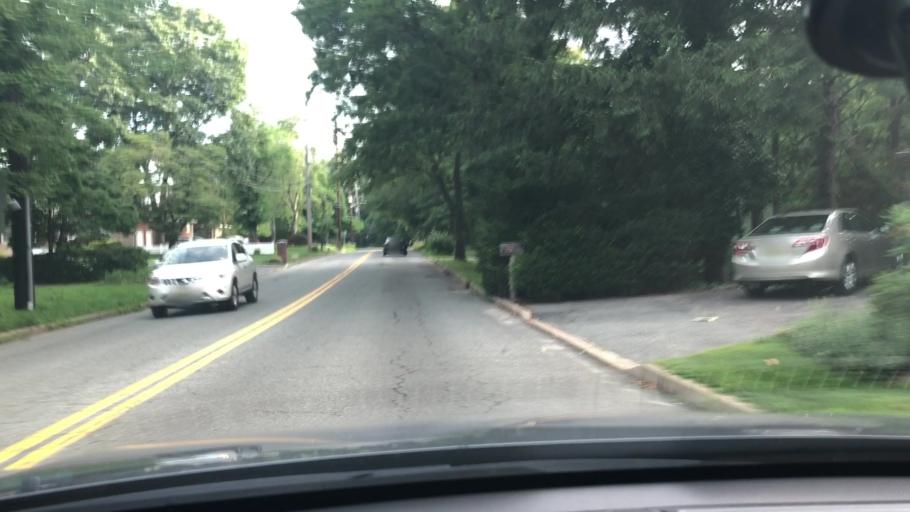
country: US
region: New Jersey
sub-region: Middlesex County
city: Milltown
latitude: 40.4365
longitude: -74.4646
